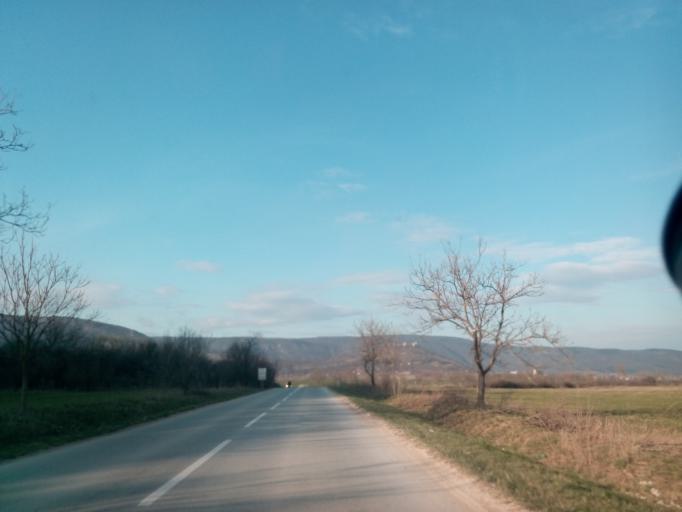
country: SK
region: Kosicky
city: Medzev
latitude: 48.5854
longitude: 20.8525
